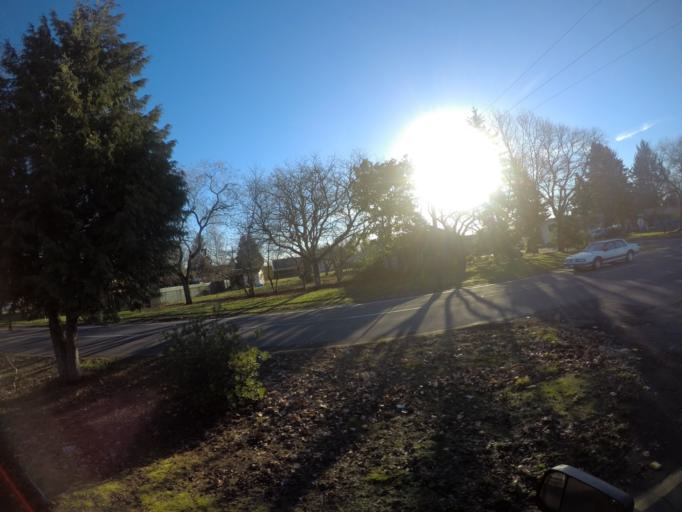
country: US
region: Washington
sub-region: Clark County
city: Walnut Grove
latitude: 45.6168
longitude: -122.5867
